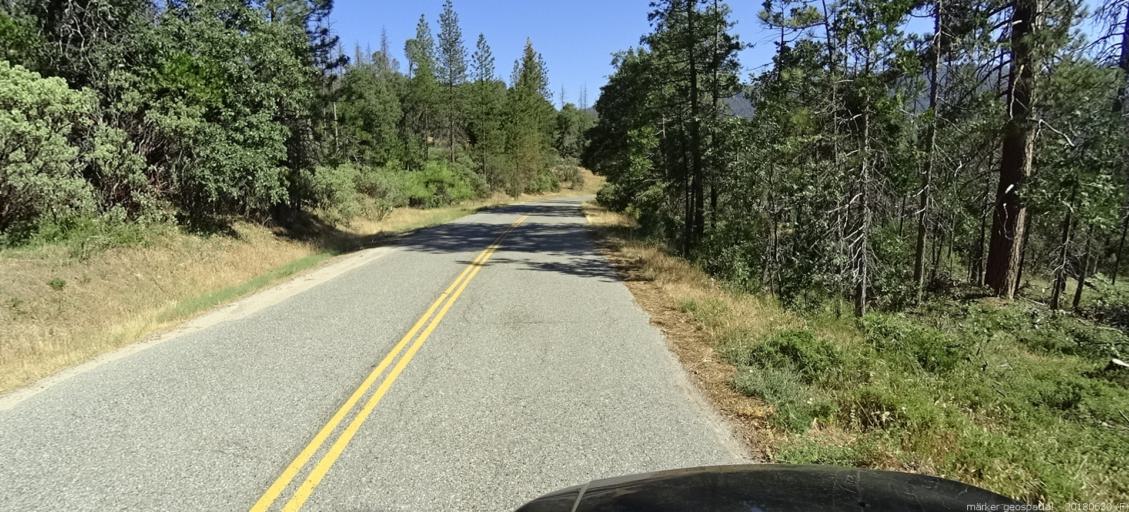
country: US
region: California
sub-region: Fresno County
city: Auberry
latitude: 37.1942
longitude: -119.4206
